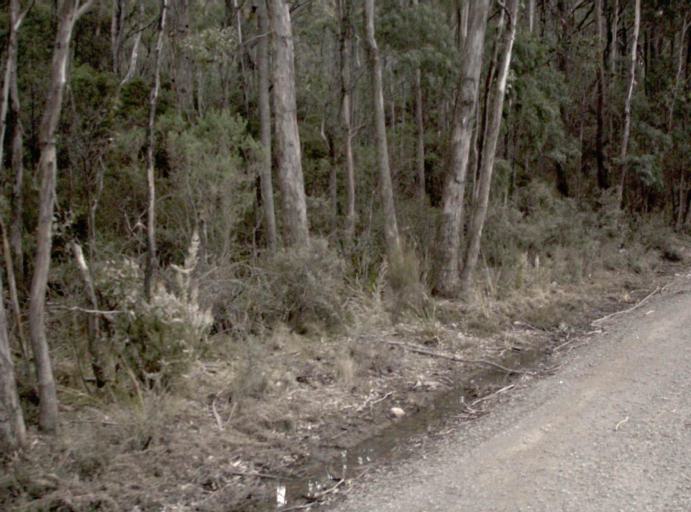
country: AU
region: Tasmania
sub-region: Launceston
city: Newstead
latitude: -41.3666
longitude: 147.2339
